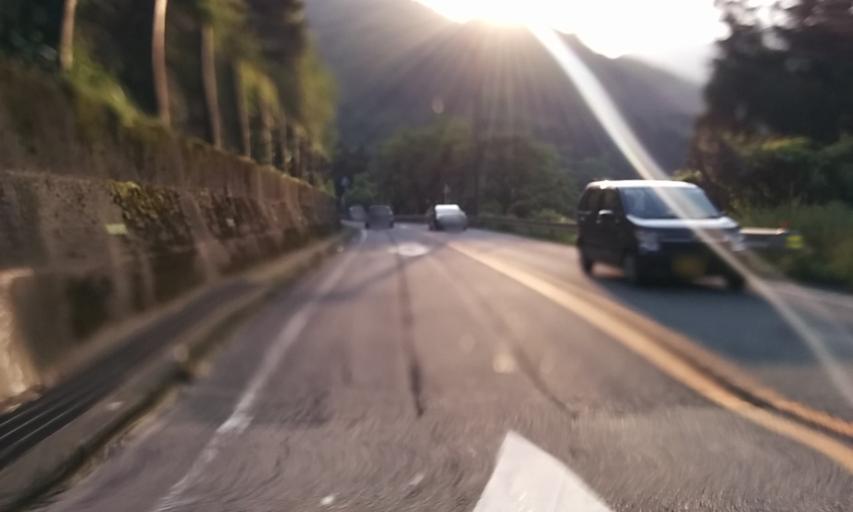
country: JP
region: Ehime
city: Saijo
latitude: 33.8439
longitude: 132.9973
